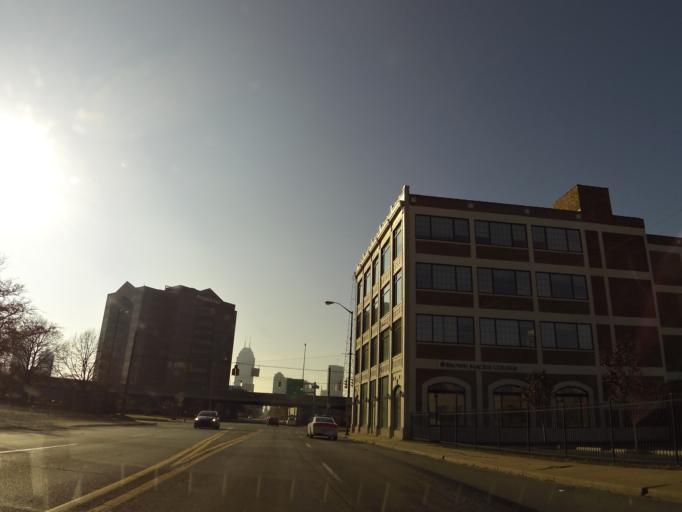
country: US
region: Indiana
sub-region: Marion County
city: Indianapolis
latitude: 39.7838
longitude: -86.1574
